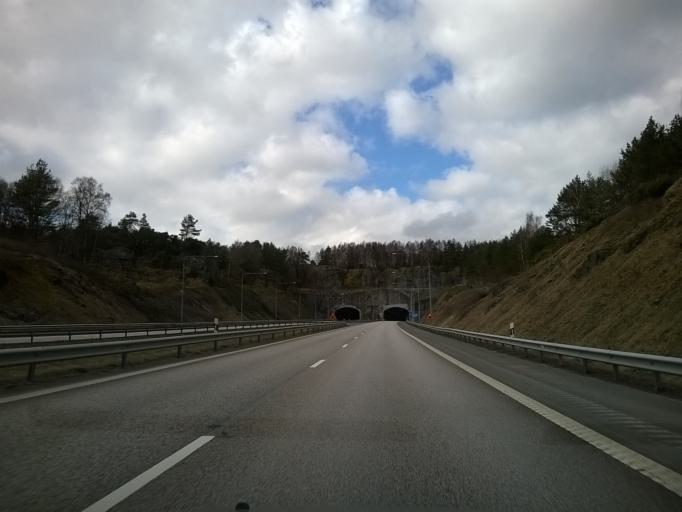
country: SE
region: Halland
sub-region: Varbergs Kommun
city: Veddige
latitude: 57.2330
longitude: 12.2254
